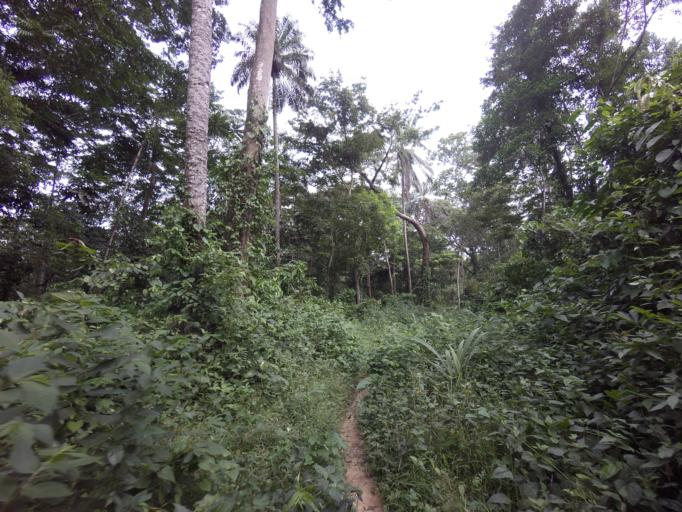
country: SL
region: Eastern Province
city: Tombodu
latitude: 8.1608
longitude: -10.6292
